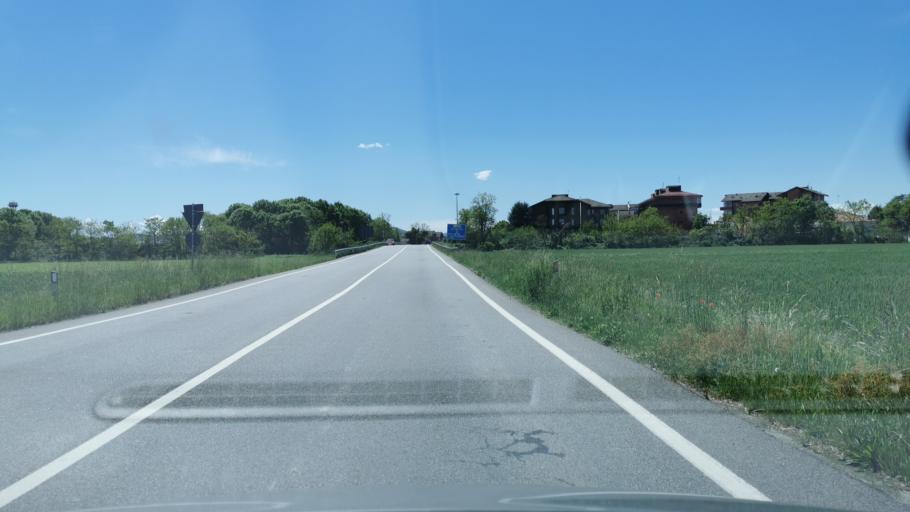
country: IT
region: Piedmont
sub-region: Provincia di Torino
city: Volpiano
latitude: 45.1991
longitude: 7.7901
